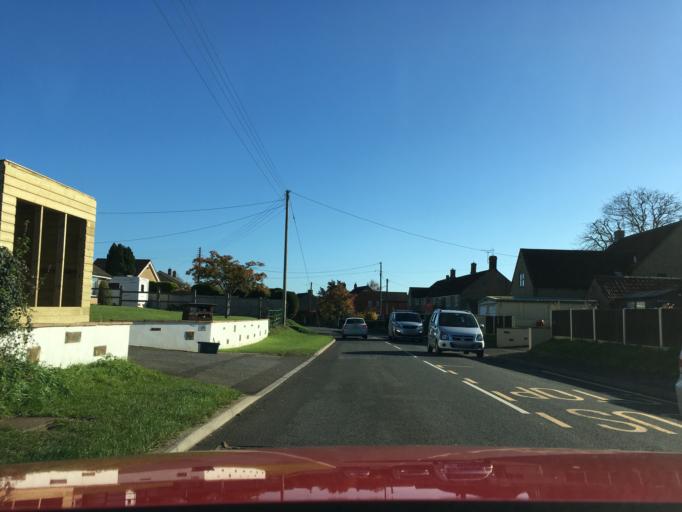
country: GB
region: England
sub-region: Somerset
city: Stoke-sub-Hamdon
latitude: 50.9713
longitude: -2.7167
